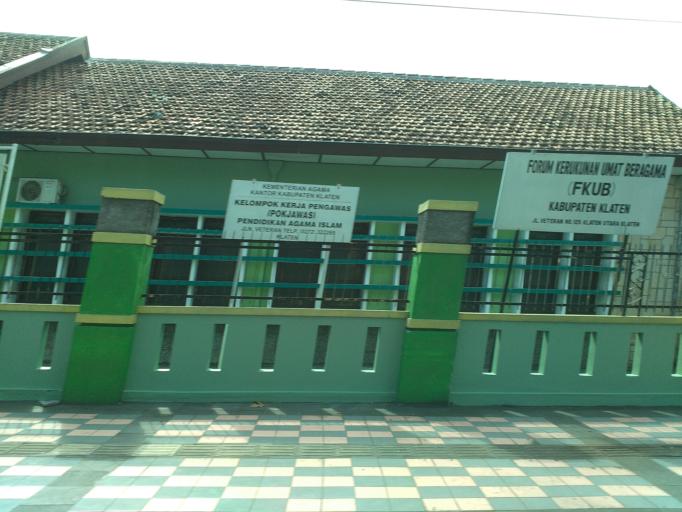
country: ID
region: Central Java
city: Klaten
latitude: -7.6950
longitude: 110.6096
